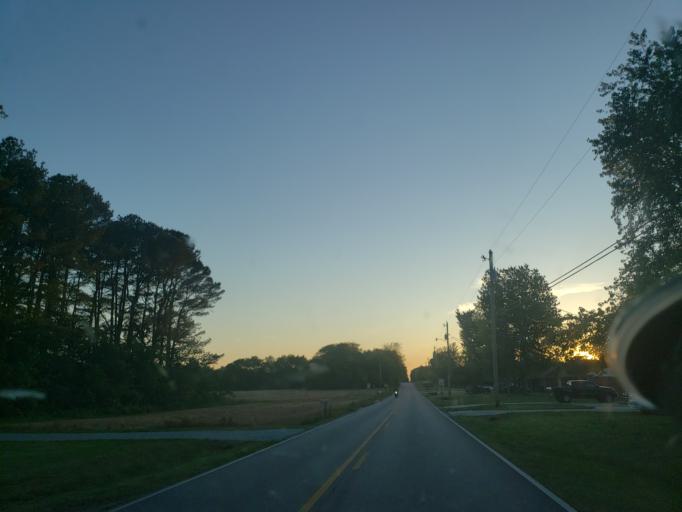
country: US
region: Alabama
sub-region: Madison County
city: Hazel Green
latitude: 34.9769
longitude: -86.6209
